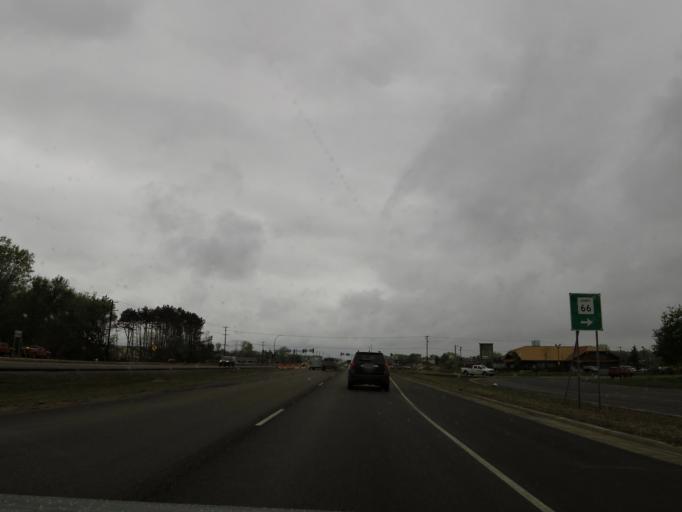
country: US
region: Minnesota
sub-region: Washington County
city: Stillwater
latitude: 45.0361
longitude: -92.8179
